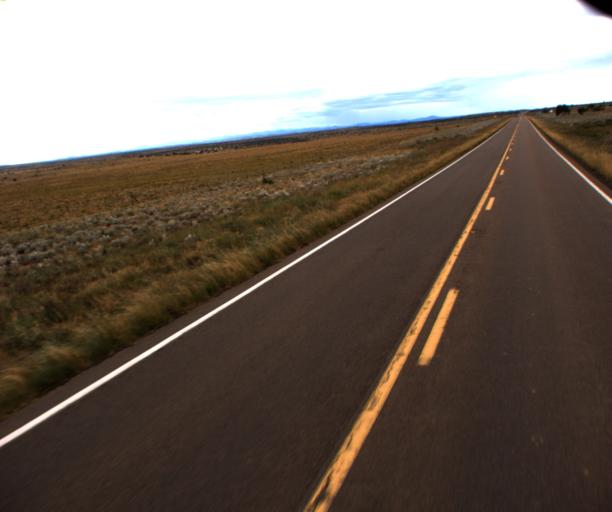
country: US
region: Arizona
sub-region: Navajo County
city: Snowflake
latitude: 34.6045
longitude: -110.0890
